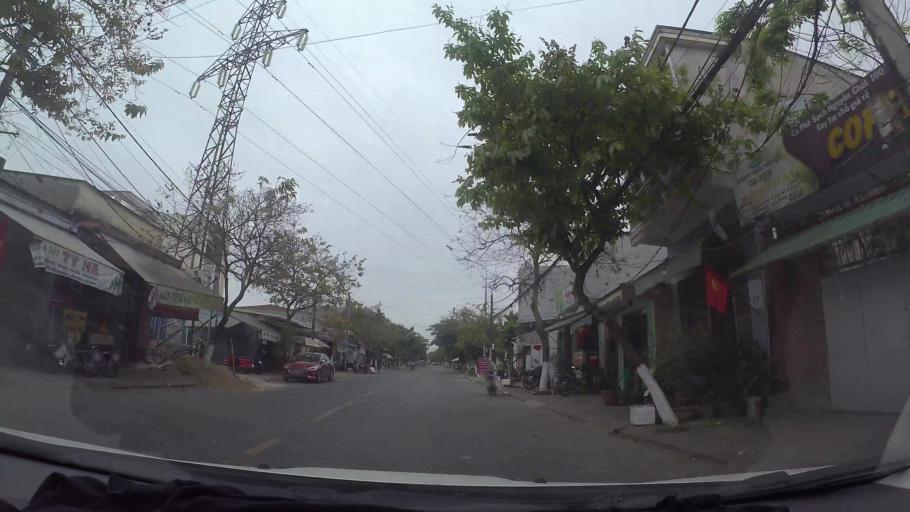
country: VN
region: Da Nang
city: Lien Chieu
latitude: 16.0652
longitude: 108.1496
